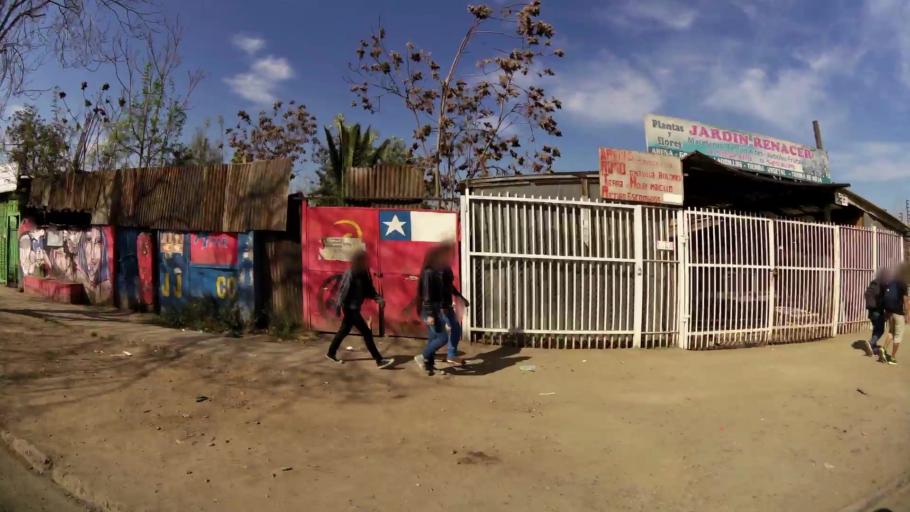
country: CL
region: Santiago Metropolitan
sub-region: Provincia de Santiago
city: Santiago
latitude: -33.3972
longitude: -70.6419
